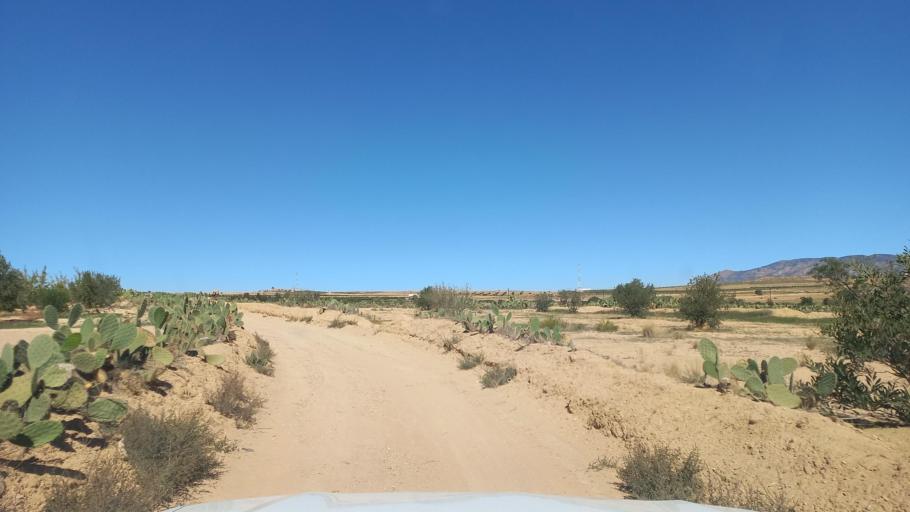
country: TN
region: Al Qasrayn
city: Sbiba
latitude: 35.3645
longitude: 9.0893
